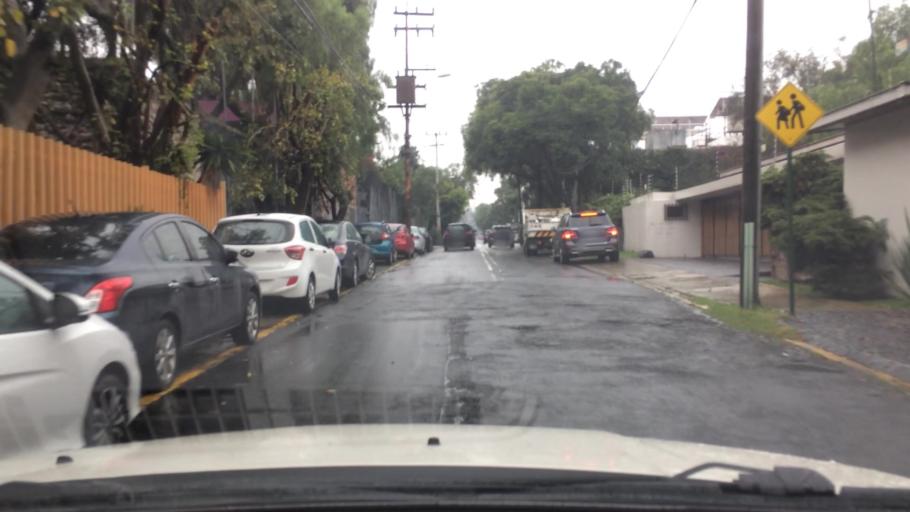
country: MX
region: Mexico City
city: Magdalena Contreras
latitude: 19.3257
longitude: -99.2040
